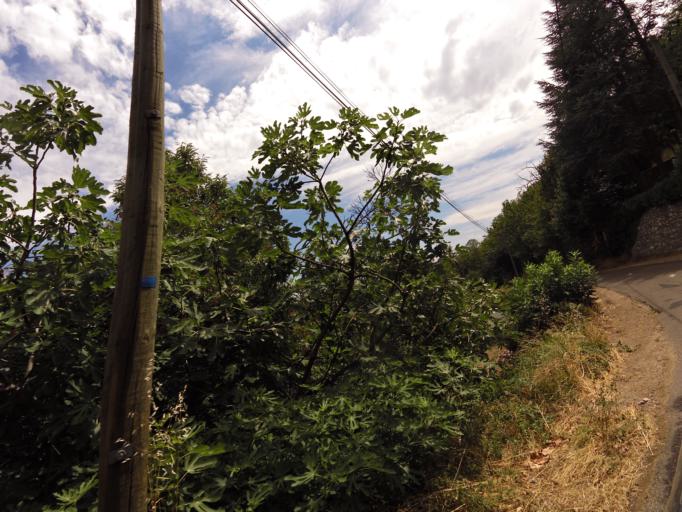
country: FR
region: Languedoc-Roussillon
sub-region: Departement du Gard
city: Le Vigan
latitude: 44.0225
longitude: 3.6243
